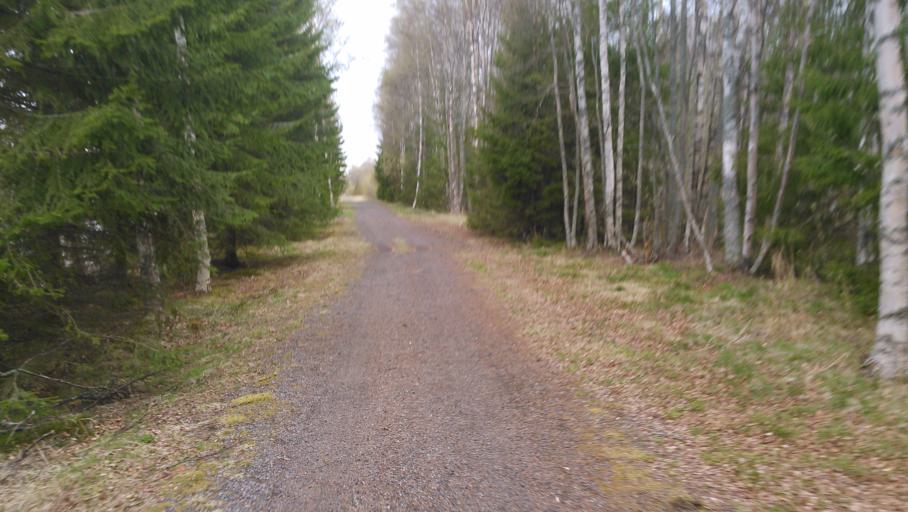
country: SE
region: Vaesterbotten
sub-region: Umea Kommun
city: Umea
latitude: 63.7822
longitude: 20.3159
